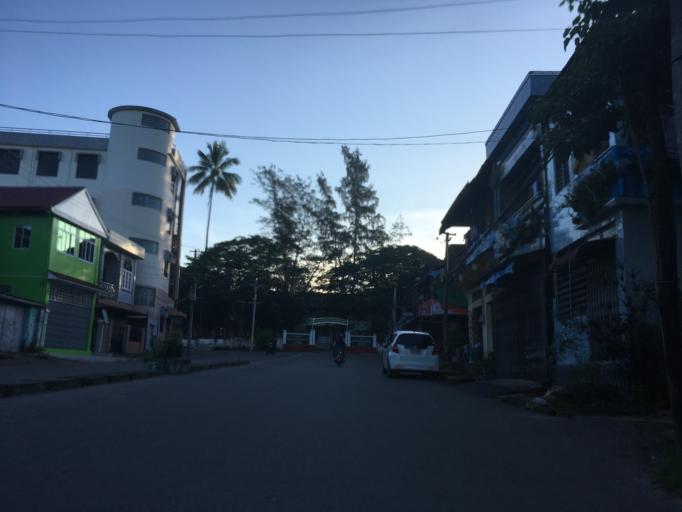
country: MM
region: Mon
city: Mawlamyine
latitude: 16.4708
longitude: 97.6249
